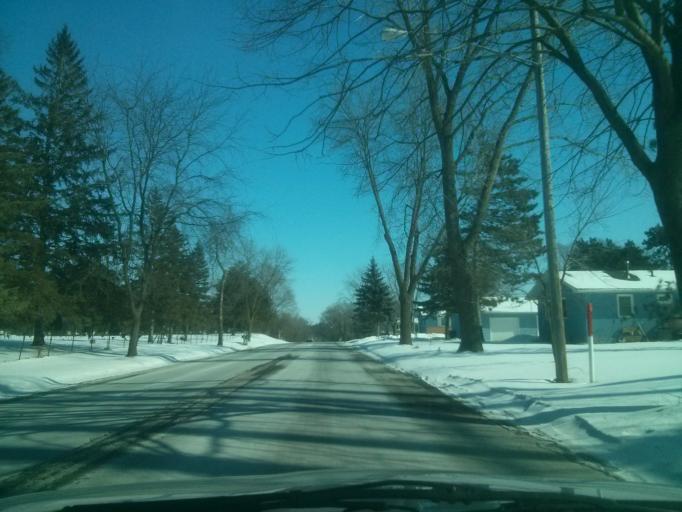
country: US
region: Wisconsin
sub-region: Saint Croix County
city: Hudson
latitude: 44.9728
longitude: -92.7453
